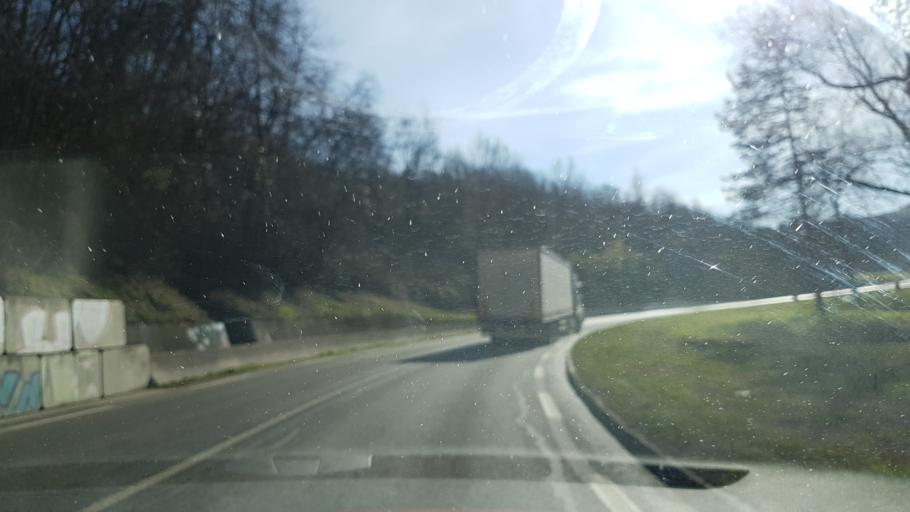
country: FR
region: Rhone-Alpes
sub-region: Departement de la Haute-Savoie
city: Frangy
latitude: 46.0236
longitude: 5.9097
